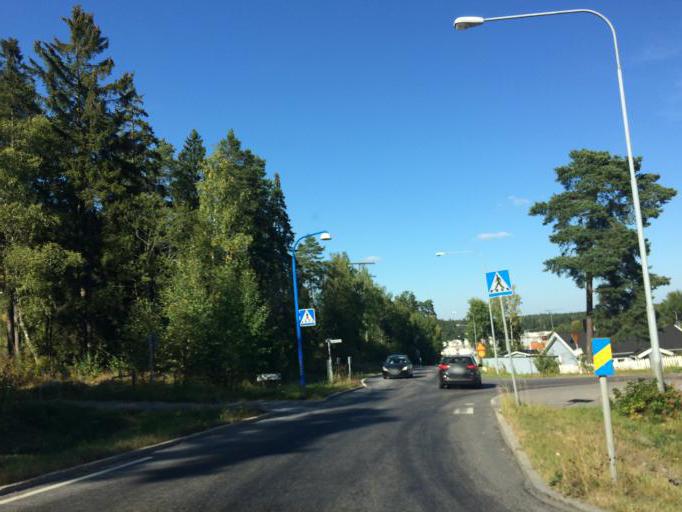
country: SE
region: Stockholm
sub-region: Upplands Vasby Kommun
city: Upplands Vaesby
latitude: 59.5032
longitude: 17.9492
